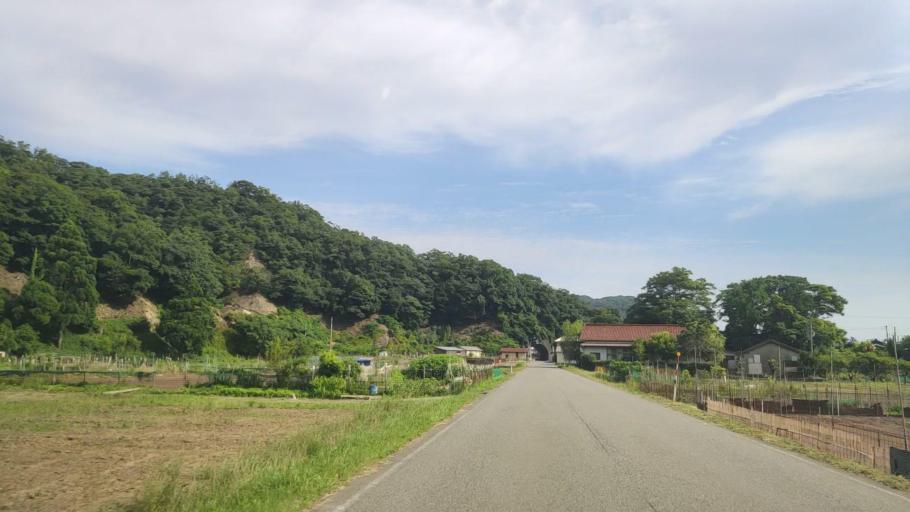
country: JP
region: Hyogo
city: Toyooka
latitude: 35.6374
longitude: 134.8363
